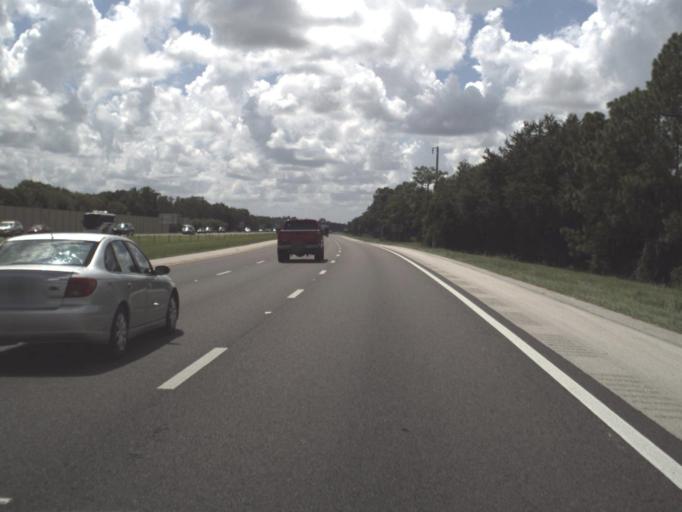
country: US
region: Florida
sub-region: Lee County
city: Bonita Springs
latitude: 26.3197
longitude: -81.7476
